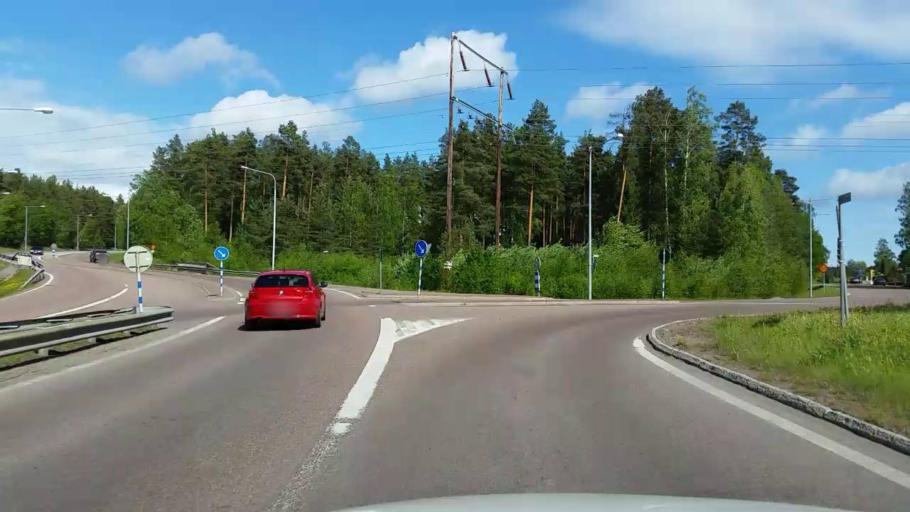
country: SE
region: Dalarna
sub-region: Faluns Kommun
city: Falun
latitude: 60.5988
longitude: 15.6713
